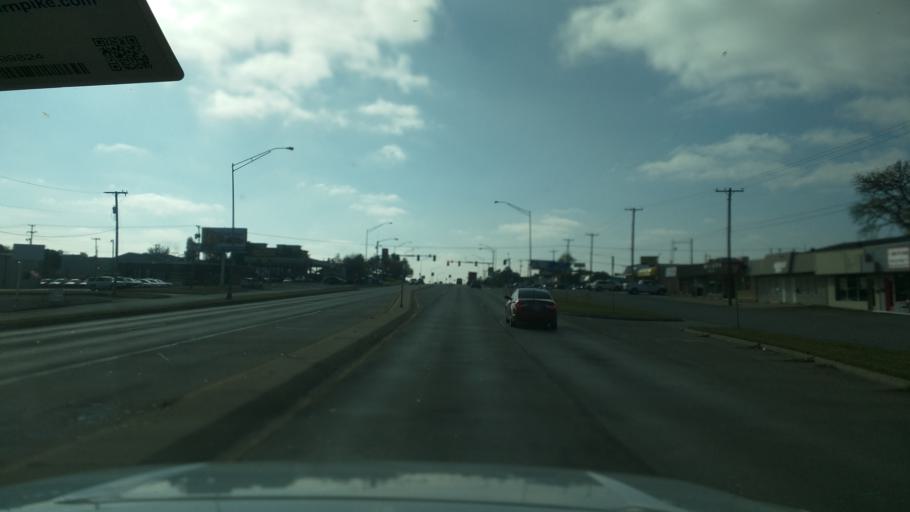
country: US
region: Oklahoma
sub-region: Washington County
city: Dewey
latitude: 36.7587
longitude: -95.9356
